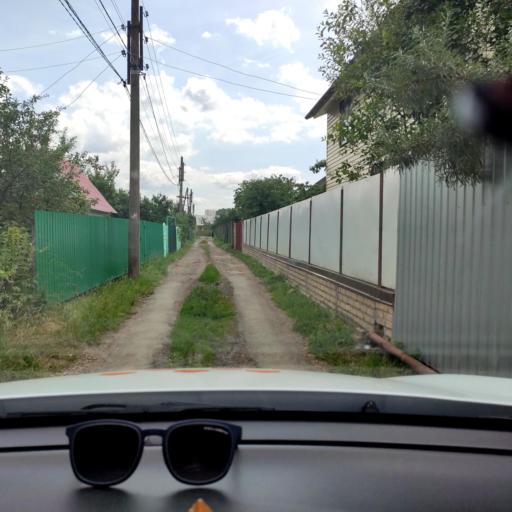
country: RU
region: Tatarstan
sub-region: Gorod Kazan'
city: Kazan
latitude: 55.8084
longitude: 49.2143
